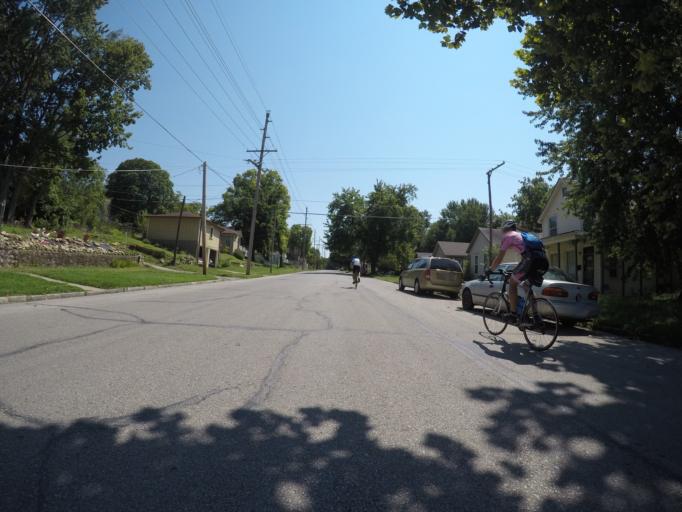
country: US
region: Kansas
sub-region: Leavenworth County
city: Leavenworth
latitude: 39.3131
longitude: -94.9095
